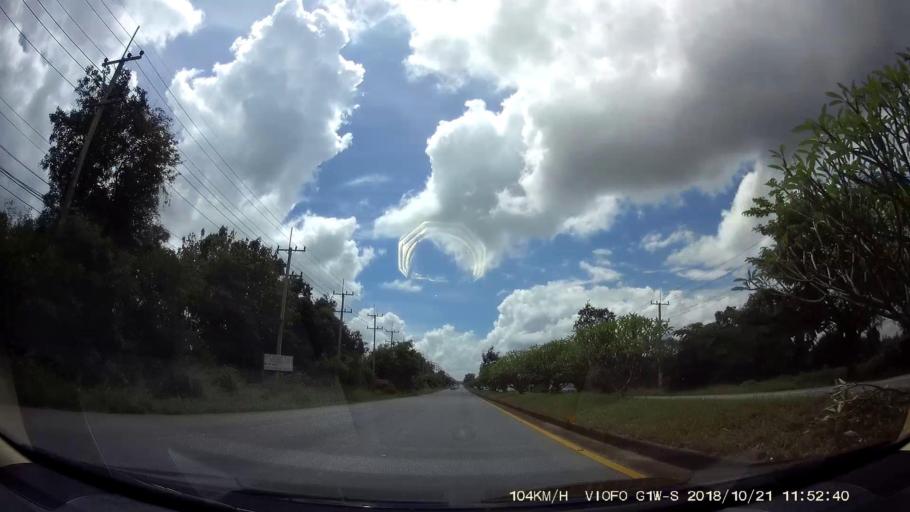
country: TH
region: Chaiyaphum
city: Chatturat
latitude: 15.6061
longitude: 101.9103
